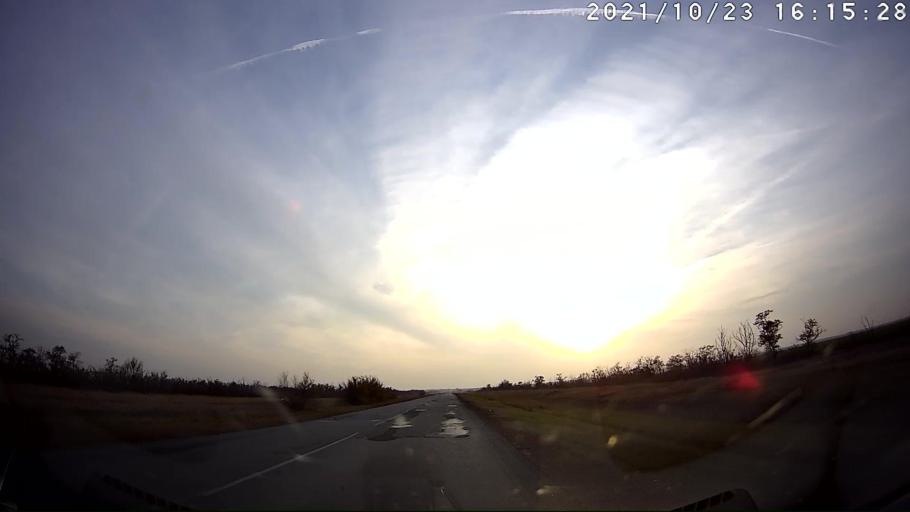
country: RU
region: Volgograd
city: Kotel'nikovo
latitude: 47.9339
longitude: 43.5935
